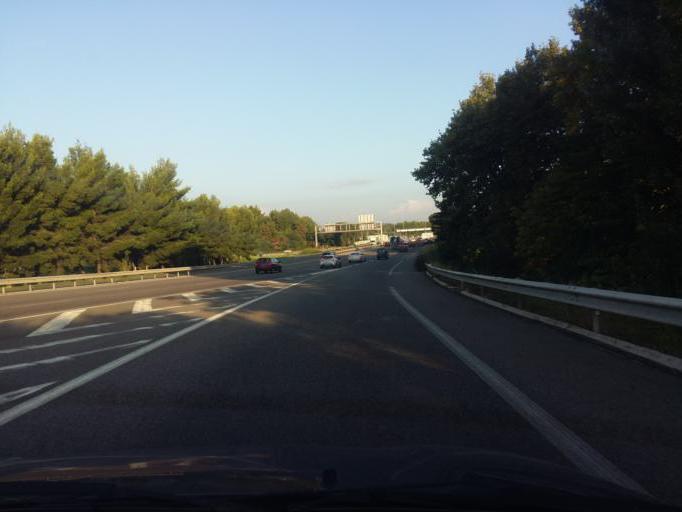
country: FR
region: Languedoc-Roussillon
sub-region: Departement du Gard
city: Nimes
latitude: 43.8117
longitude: 4.3459
